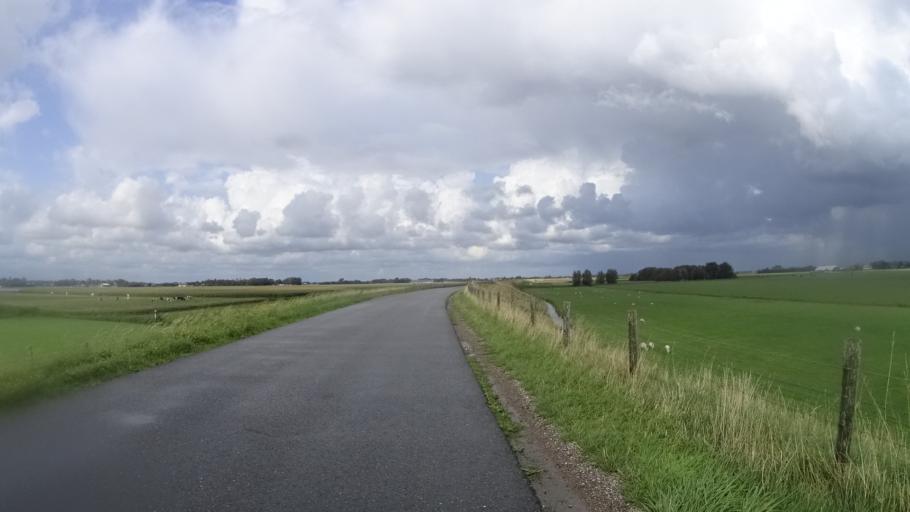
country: NL
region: North Holland
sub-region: Gemeente Schagen
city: Harenkarspel
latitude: 52.7789
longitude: 4.7432
